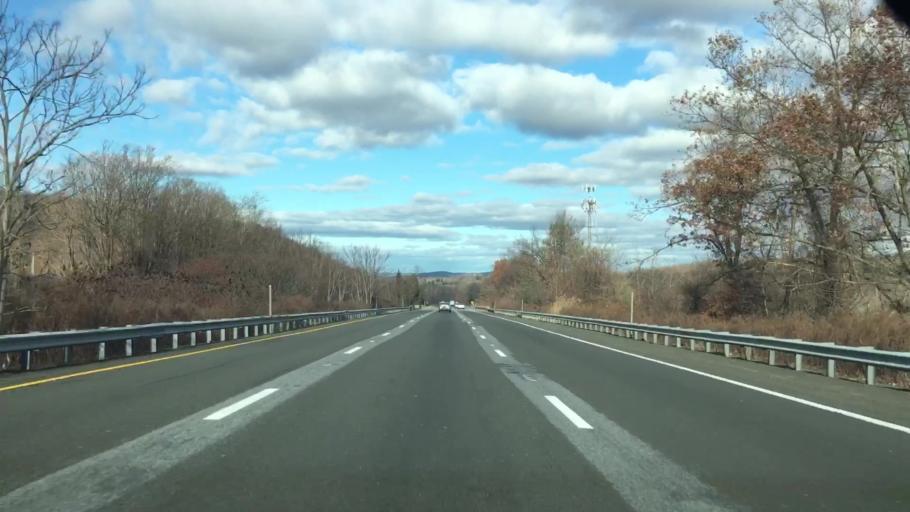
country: US
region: New York
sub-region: Westchester County
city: Mount Kisco
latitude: 41.1931
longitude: -73.6867
